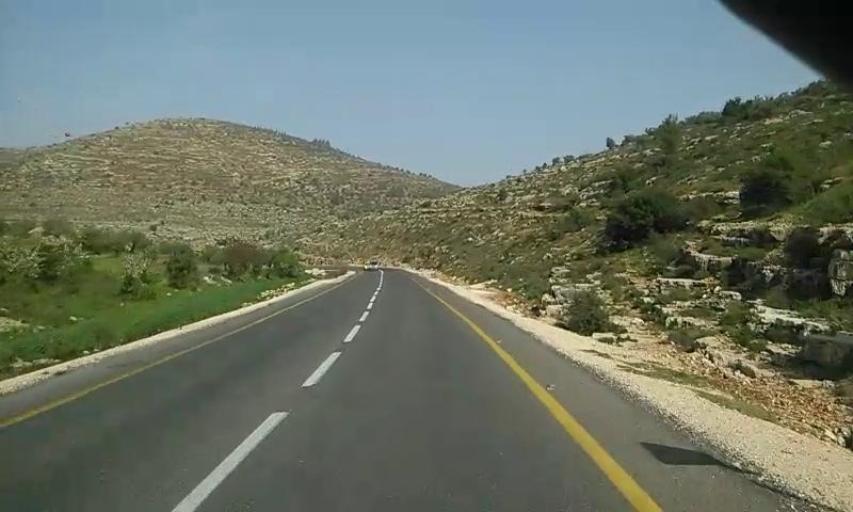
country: PS
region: West Bank
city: `Atarah
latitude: 31.9959
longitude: 35.2261
